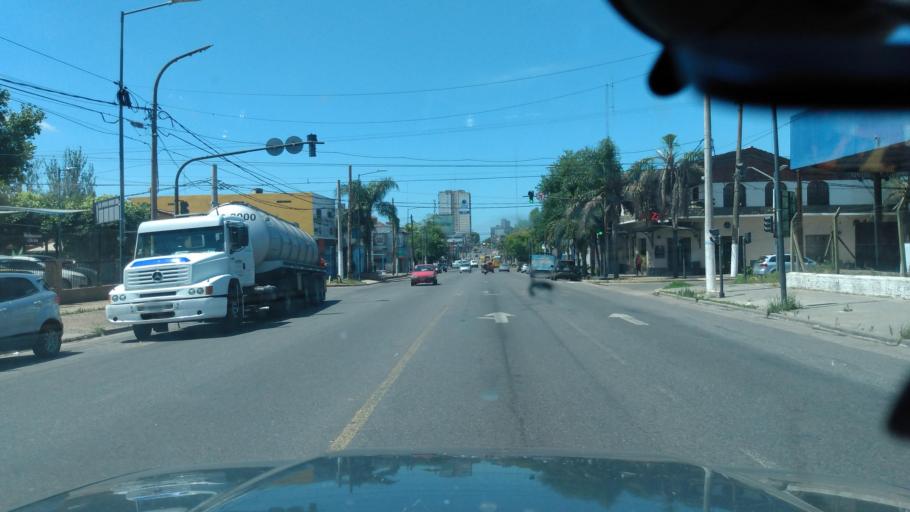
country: AR
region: Buenos Aires
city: Hurlingham
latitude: -34.5484
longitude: -58.7186
